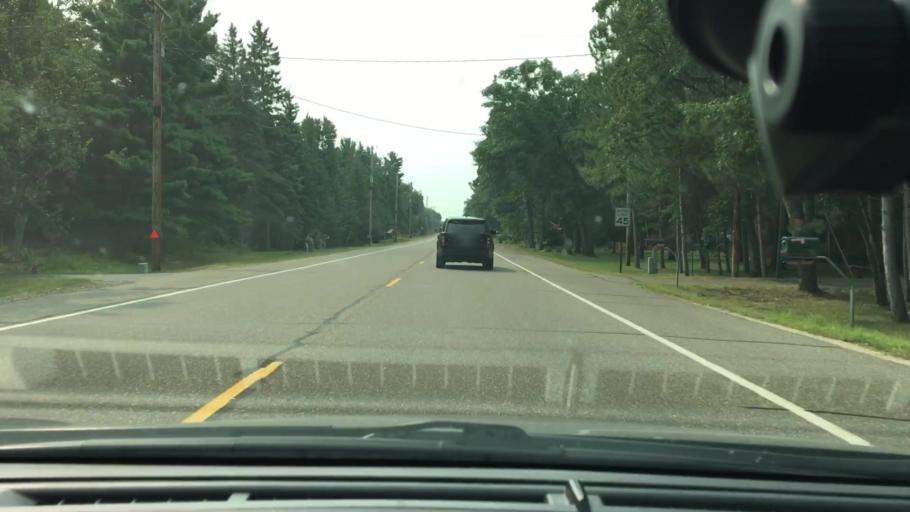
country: US
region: Minnesota
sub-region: Crow Wing County
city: Cross Lake
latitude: 46.5879
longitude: -94.1316
